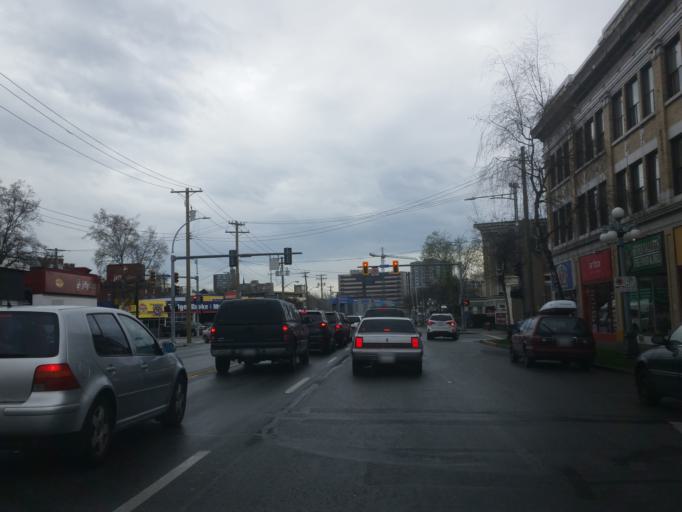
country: CA
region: British Columbia
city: Victoria
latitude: 48.4362
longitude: -123.3659
